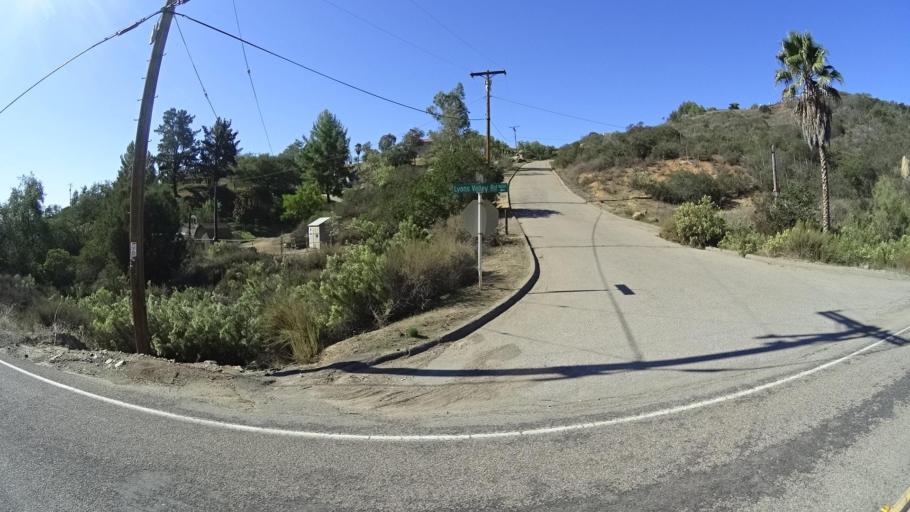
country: US
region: California
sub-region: San Diego County
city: Jamul
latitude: 32.7141
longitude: -116.8011
